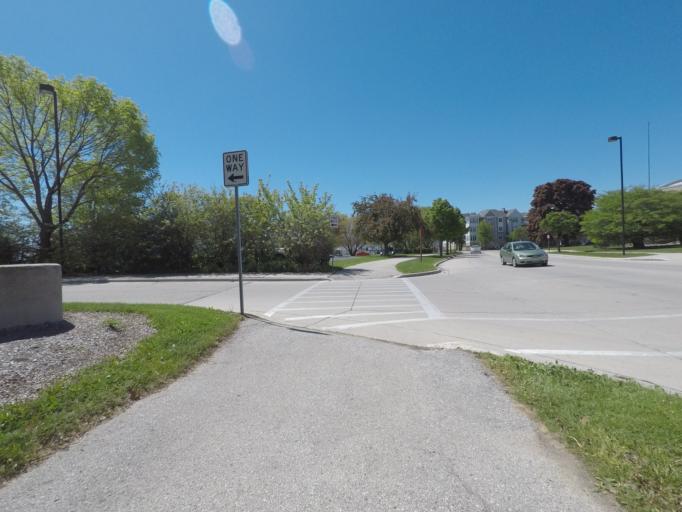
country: US
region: Wisconsin
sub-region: Sheboygan County
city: Sheboygan
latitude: 43.7508
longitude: -87.7041
